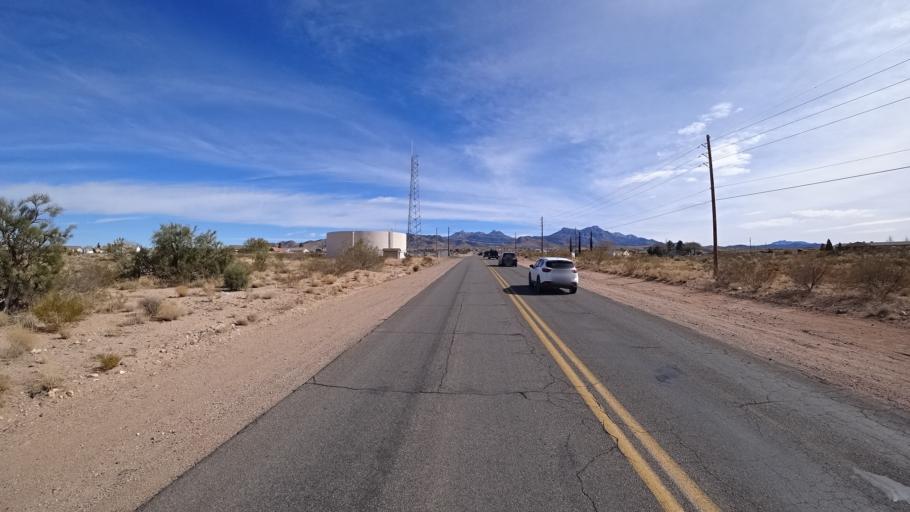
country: US
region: Arizona
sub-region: Mohave County
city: Kingman
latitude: 35.1852
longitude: -114.0048
